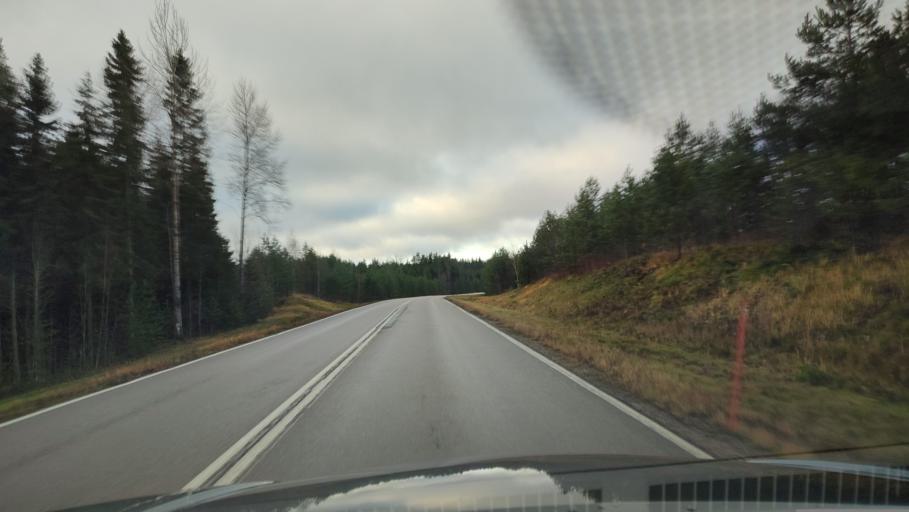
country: FI
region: Ostrobothnia
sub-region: Sydosterbotten
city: Kristinestad
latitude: 62.3064
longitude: 21.4423
